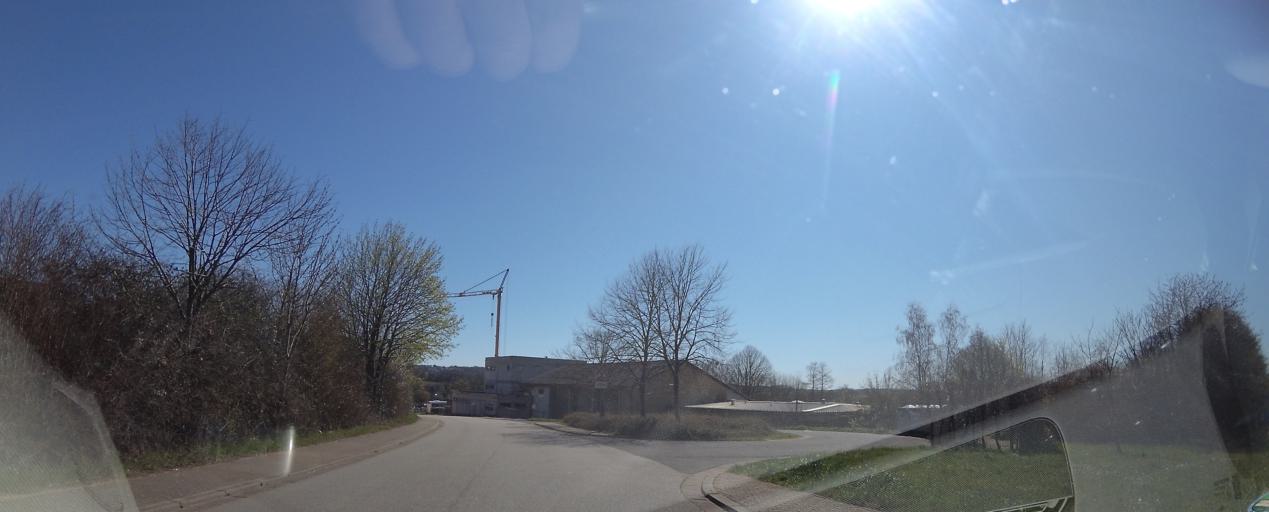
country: DE
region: Saarland
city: Heusweiler
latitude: 49.3516
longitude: 6.9795
